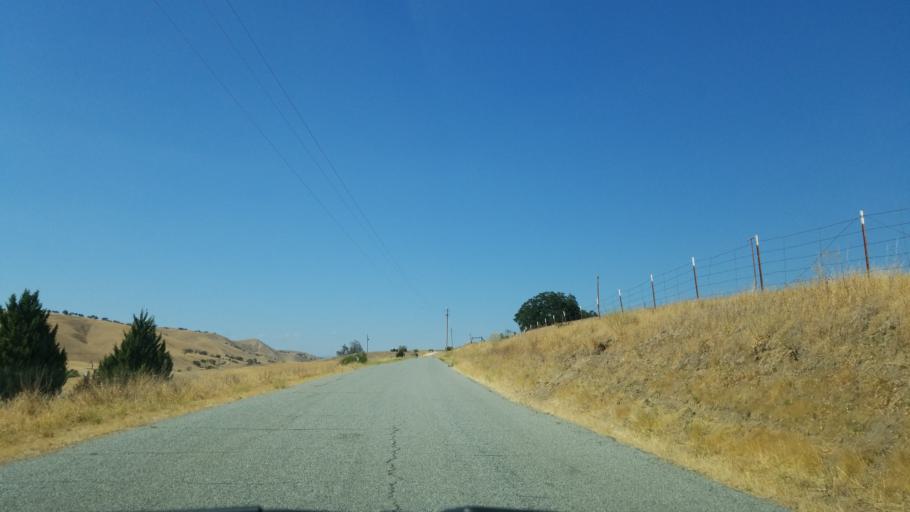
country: US
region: California
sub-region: San Luis Obispo County
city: San Miguel
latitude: 35.7988
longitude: -120.7155
